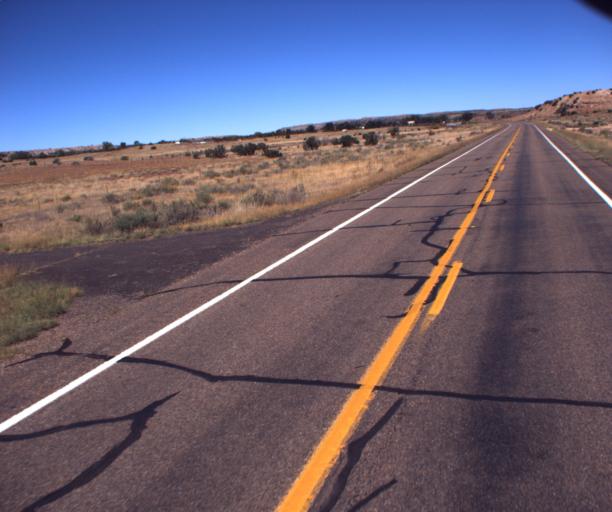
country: US
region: Arizona
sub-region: Apache County
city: Saint Johns
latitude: 34.4235
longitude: -109.4111
